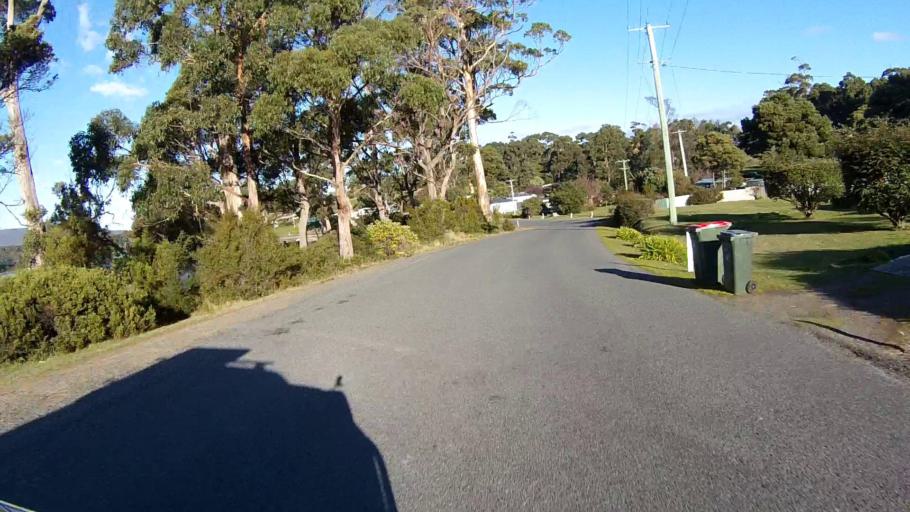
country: AU
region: Tasmania
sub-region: Clarence
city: Sandford
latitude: -43.1613
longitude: 147.8542
